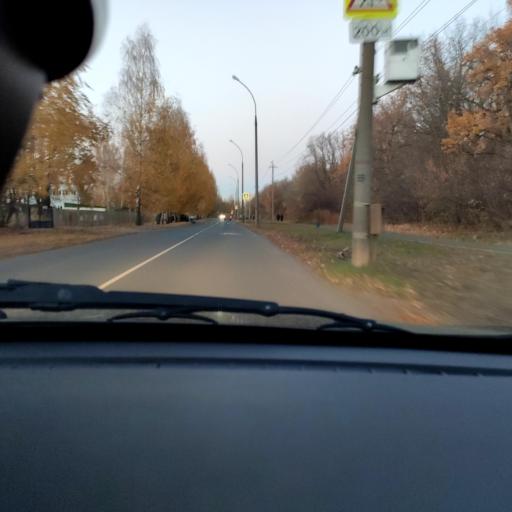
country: RU
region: Samara
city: Tol'yatti
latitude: 53.5091
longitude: 49.3077
